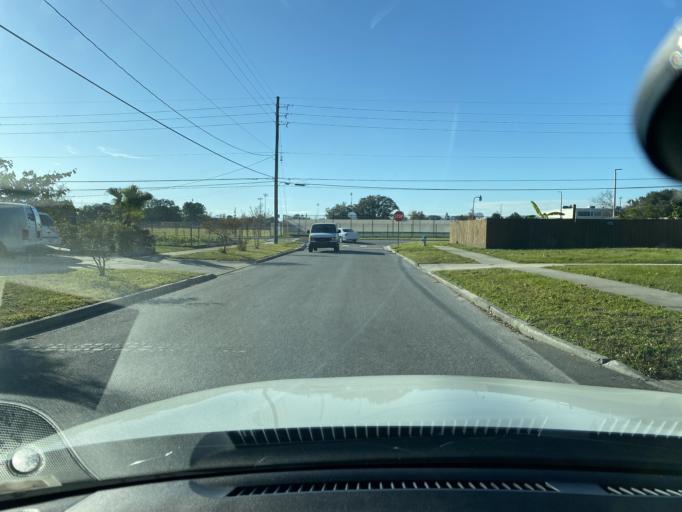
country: US
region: Florida
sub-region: Orange County
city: Azalea Park
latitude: 28.5323
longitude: -81.3019
